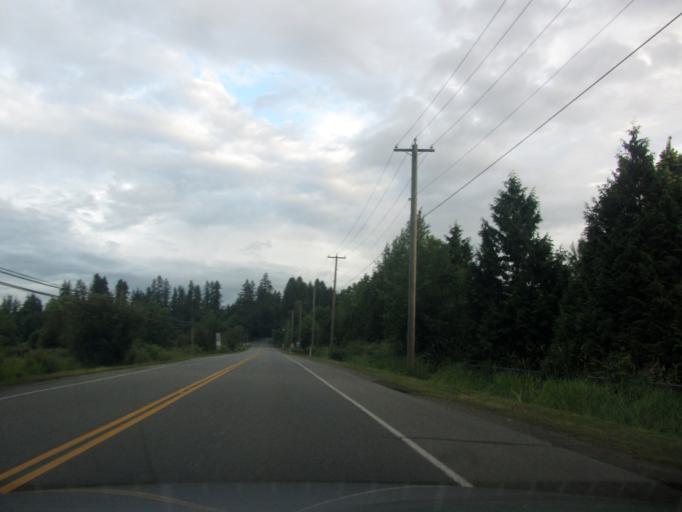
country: CA
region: British Columbia
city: Walnut Grove
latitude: 49.1563
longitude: -122.5910
